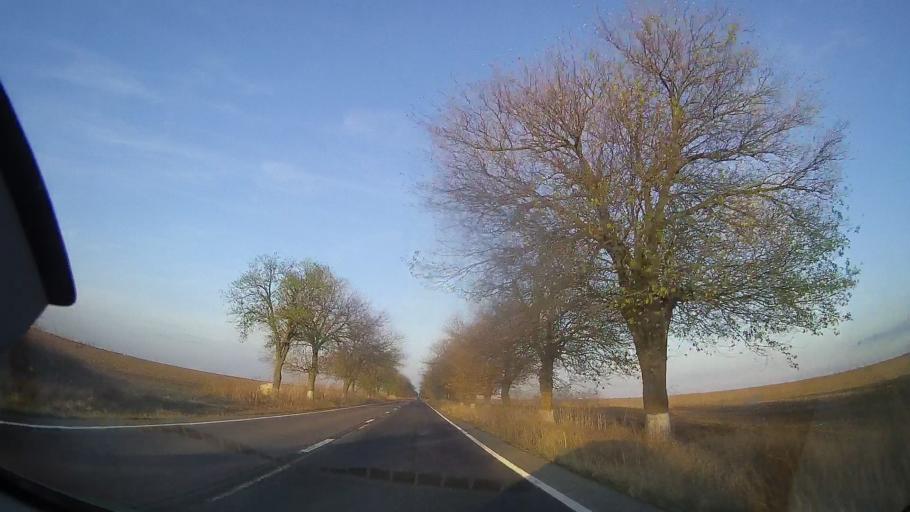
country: RO
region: Constanta
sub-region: Comuna Comana
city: Comana
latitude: 43.9032
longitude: 28.3286
